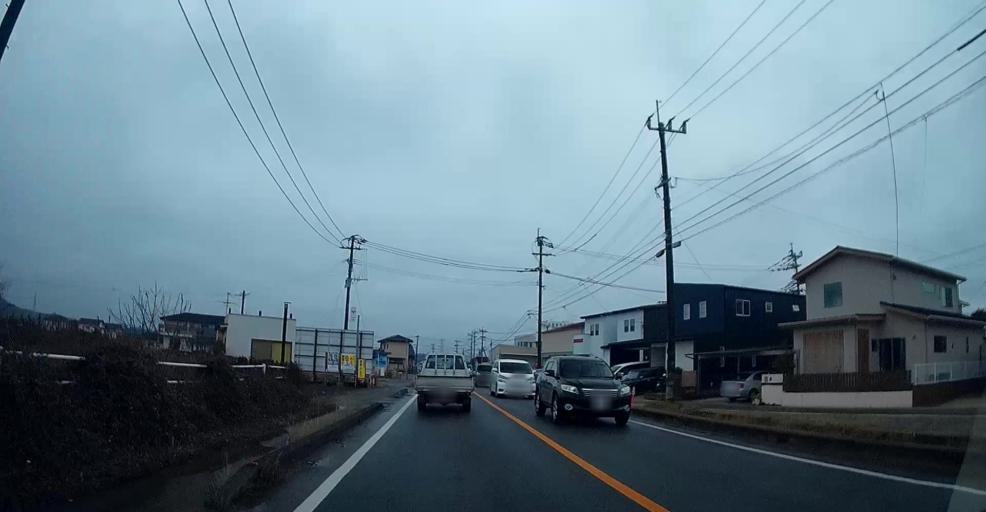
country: JP
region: Kumamoto
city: Uto
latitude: 32.7309
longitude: 130.7380
